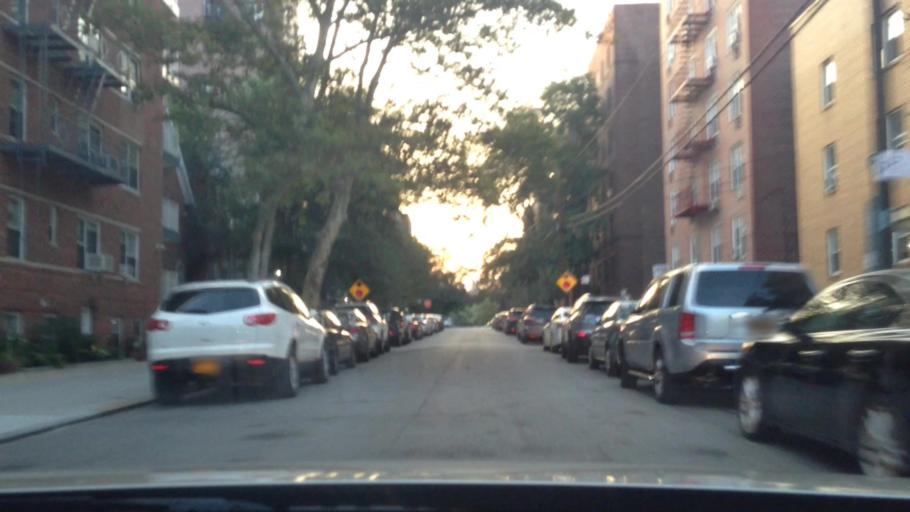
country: US
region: New York
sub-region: Queens County
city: Borough of Queens
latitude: 40.7276
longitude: -73.8603
